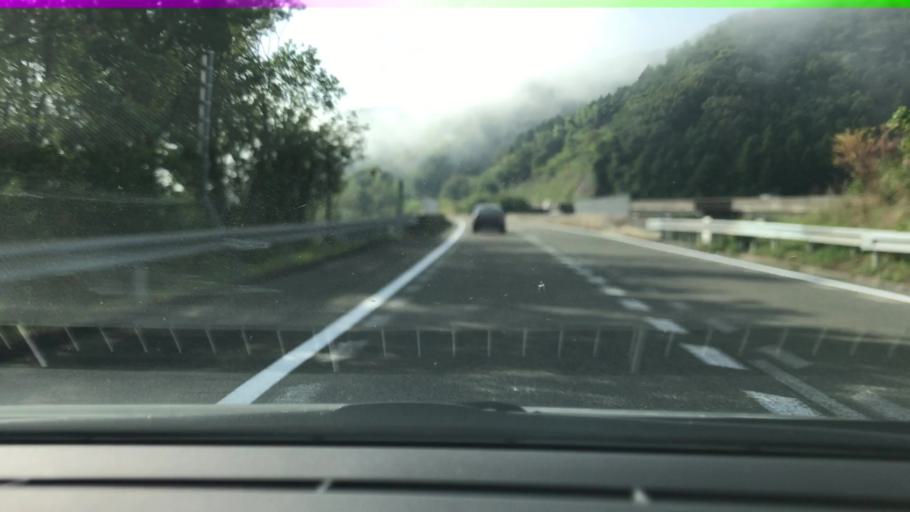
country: JP
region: Hyogo
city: Sasayama
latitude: 35.1135
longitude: 135.1657
